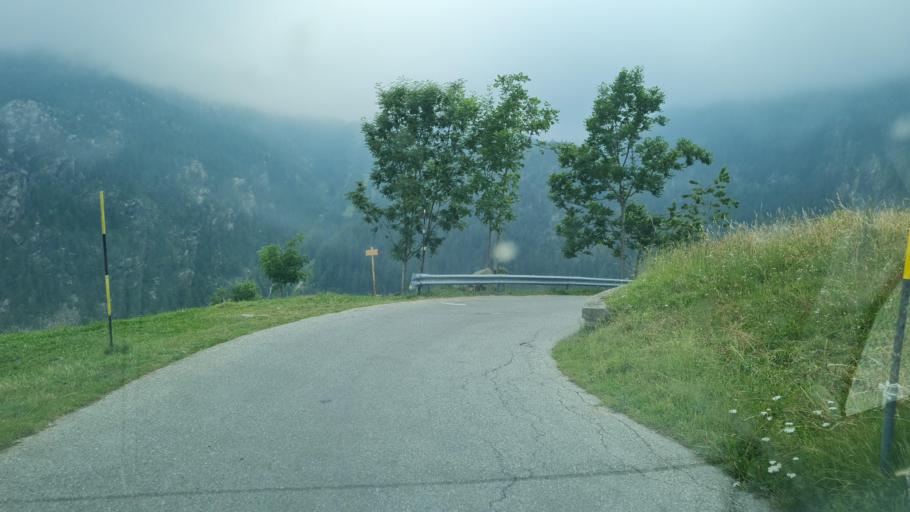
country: IT
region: Aosta Valley
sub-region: Valle d'Aosta
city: Champorcher
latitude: 45.6262
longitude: 7.6105
